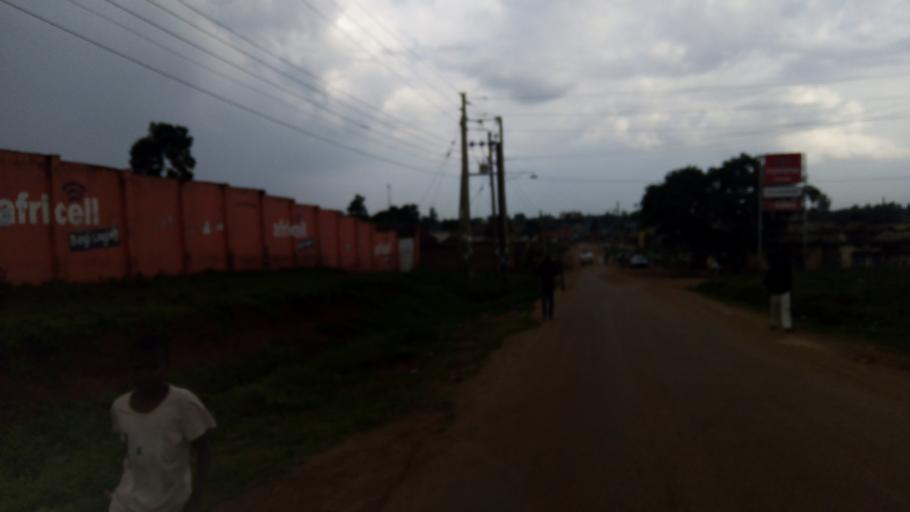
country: UG
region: Eastern Region
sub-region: Mbale District
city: Mbale
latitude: 1.0779
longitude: 34.1650
